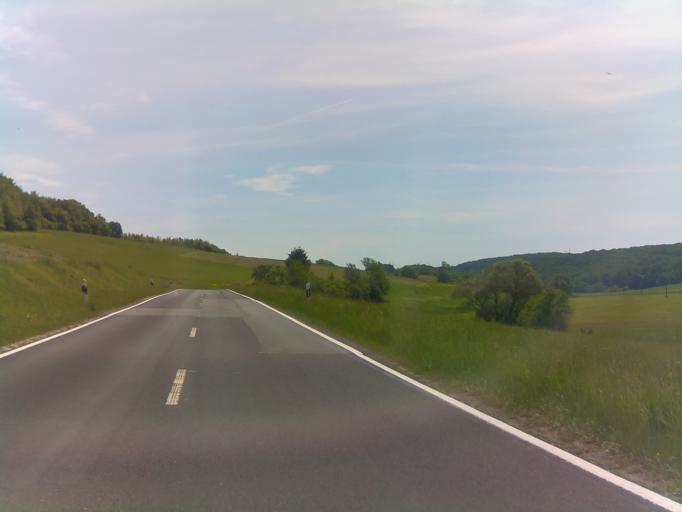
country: DE
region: Bavaria
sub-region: Regierungsbezirk Unterfranken
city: Arnstein
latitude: 50.0111
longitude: 9.9993
